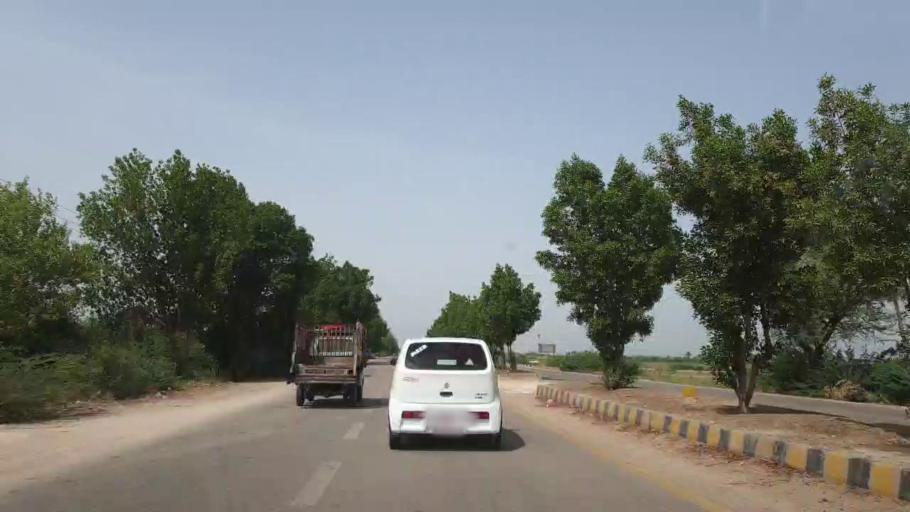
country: PK
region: Sindh
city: Sakrand
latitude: 26.1625
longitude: 68.2773
